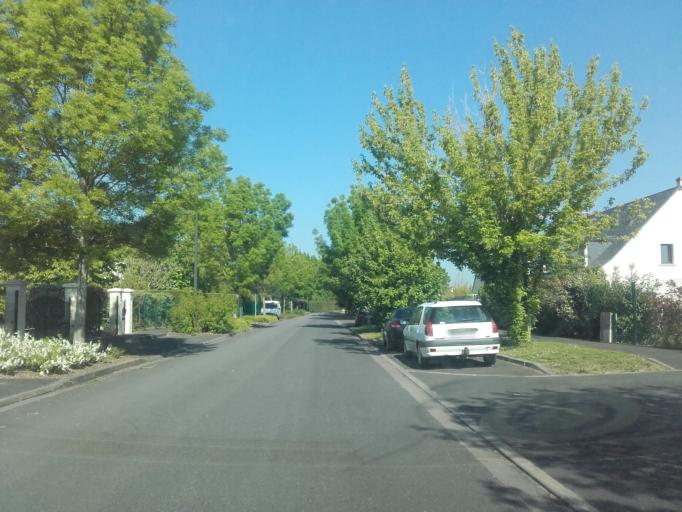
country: FR
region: Centre
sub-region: Departement d'Indre-et-Loire
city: Saint-Cyr-sur-Loire
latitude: 47.4218
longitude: 0.6710
